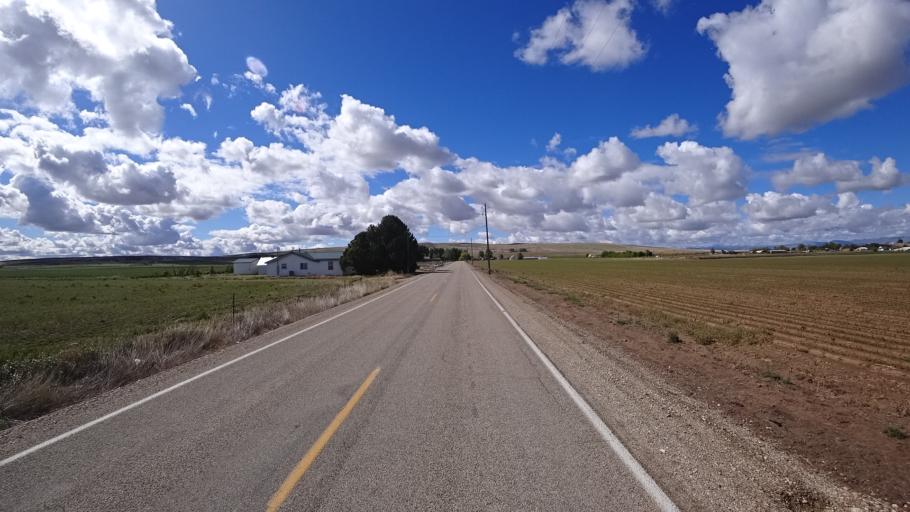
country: US
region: Idaho
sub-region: Ada County
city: Kuna
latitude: 43.4708
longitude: -116.4537
